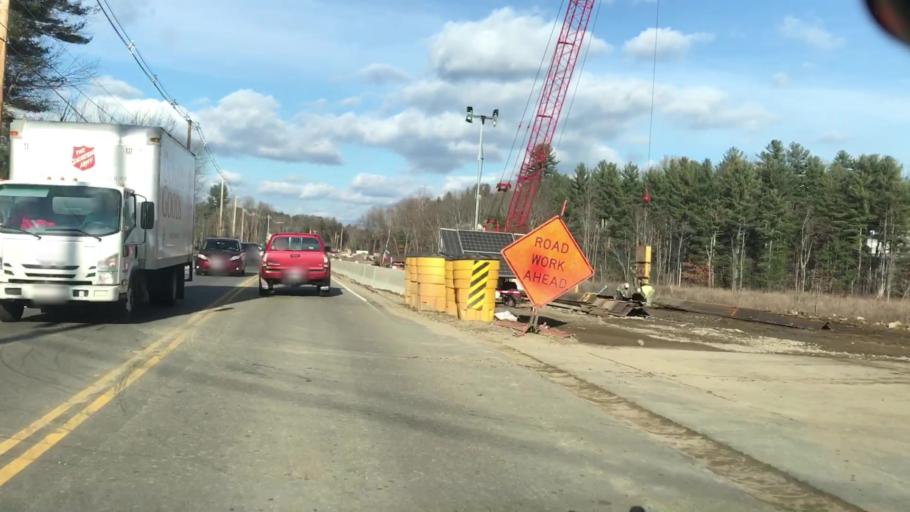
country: US
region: New Hampshire
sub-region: Hillsborough County
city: Bedford
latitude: 42.9477
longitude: -71.5126
